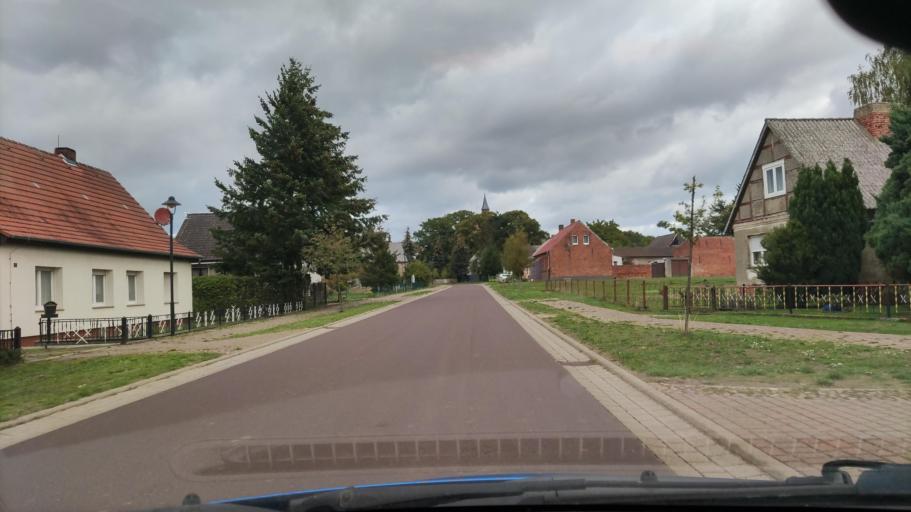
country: DE
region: Saxony-Anhalt
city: Luftkurort Arendsee
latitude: 52.8260
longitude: 11.3908
